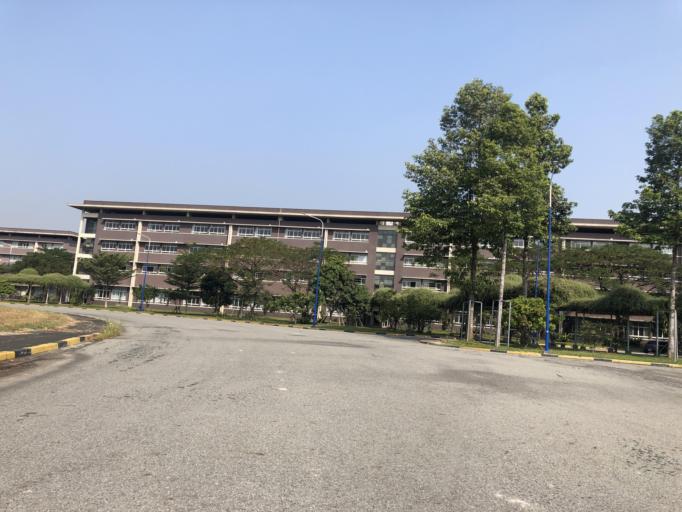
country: VN
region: Binh Duong
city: Thu Dau Mot
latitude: 11.0531
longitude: 106.6668
